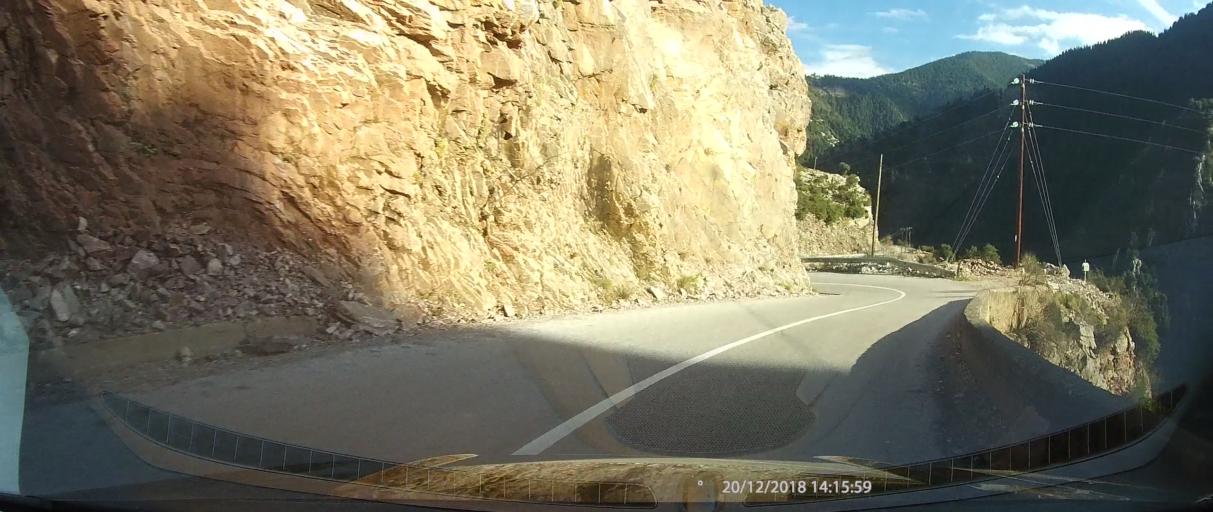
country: GR
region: West Greece
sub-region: Nomos Aitolias kai Akarnanias
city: Thermo
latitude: 38.7516
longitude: 21.6579
